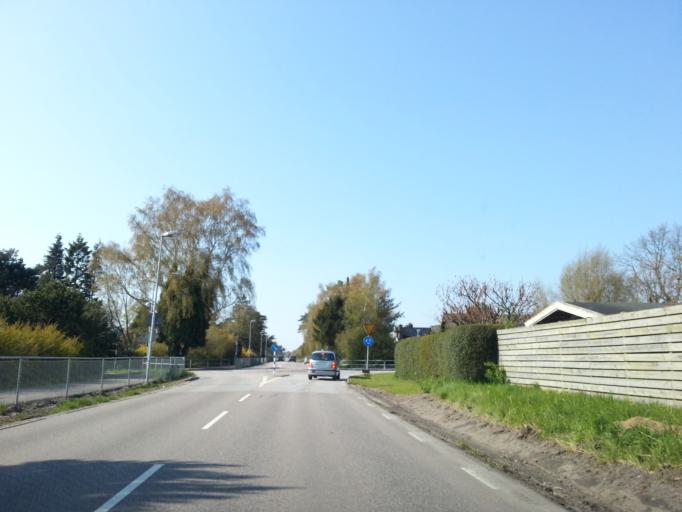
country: SE
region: Skane
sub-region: Vellinge Kommun
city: Hollviken
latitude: 55.4087
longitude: 12.9806
